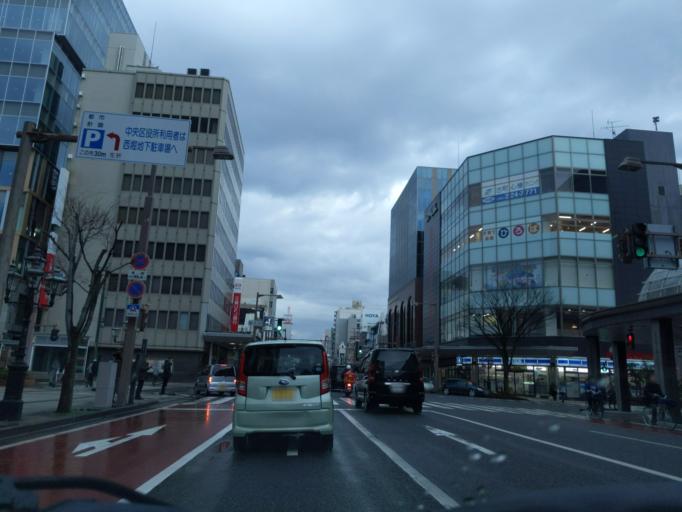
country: JP
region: Niigata
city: Niigata-shi
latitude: 37.9222
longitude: 139.0434
